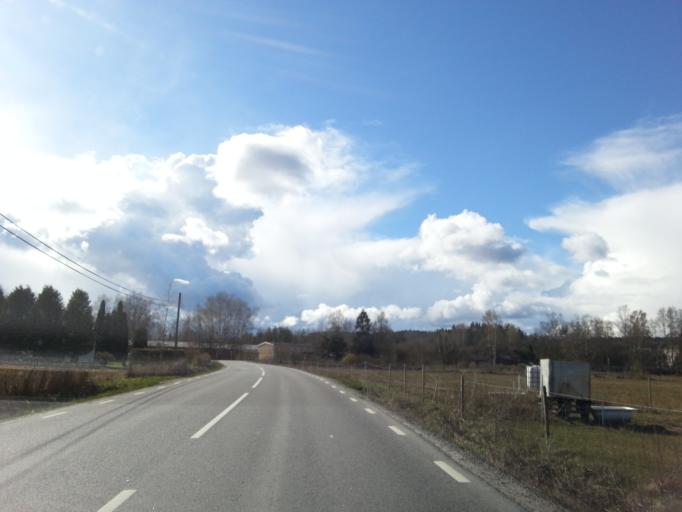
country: SE
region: Vaestra Goetaland
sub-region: Kungalvs Kommun
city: Diserod
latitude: 57.9393
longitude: 12.0226
